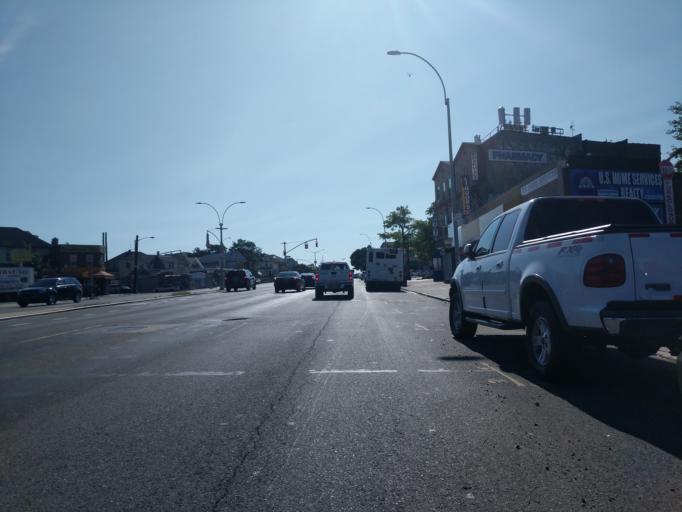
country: US
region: New York
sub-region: Queens County
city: Long Island City
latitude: 40.7617
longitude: -73.8680
